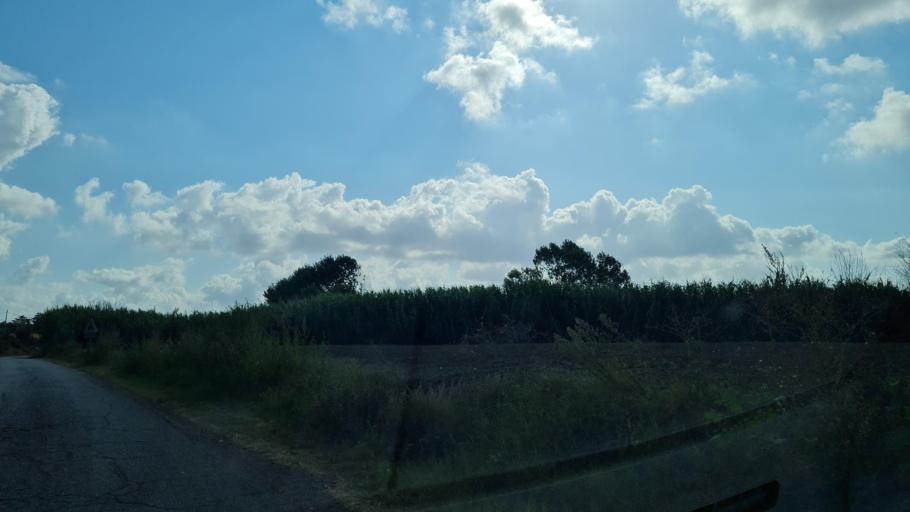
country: IT
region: Latium
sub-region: Provincia di Viterbo
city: Tarquinia
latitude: 42.2529
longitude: 11.7113
